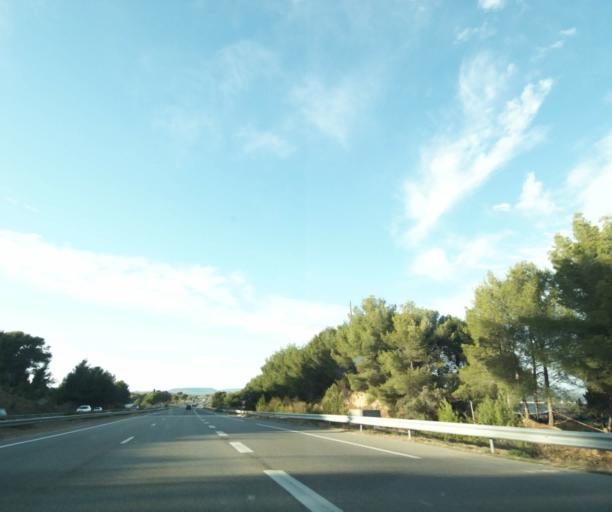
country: FR
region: Provence-Alpes-Cote d'Azur
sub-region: Departement des Bouches-du-Rhone
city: Chateauneuf-les-Martigues
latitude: 43.3962
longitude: 5.1243
